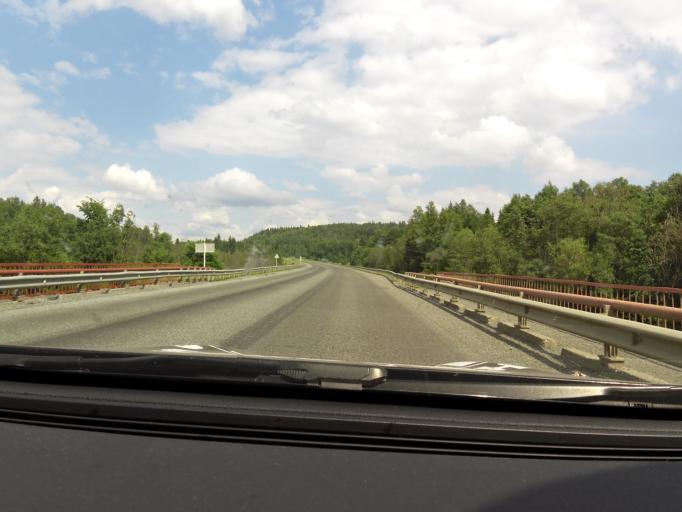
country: RU
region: Sverdlovsk
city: Ufimskiy
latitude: 56.7815
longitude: 58.4171
